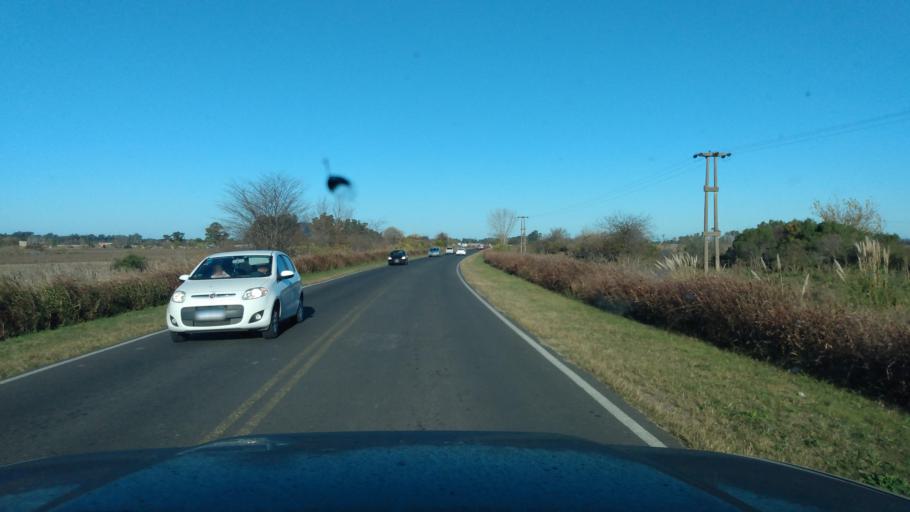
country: AR
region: Buenos Aires
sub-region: Partido de Lujan
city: Lujan
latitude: -34.5040
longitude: -59.1946
